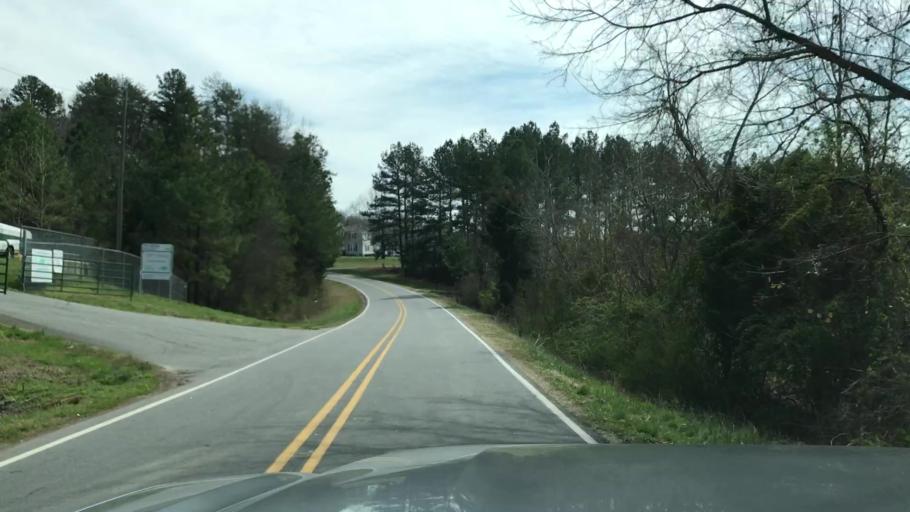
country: US
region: North Carolina
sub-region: Rutherford County
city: Spindale
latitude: 35.4453
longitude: -81.8790
